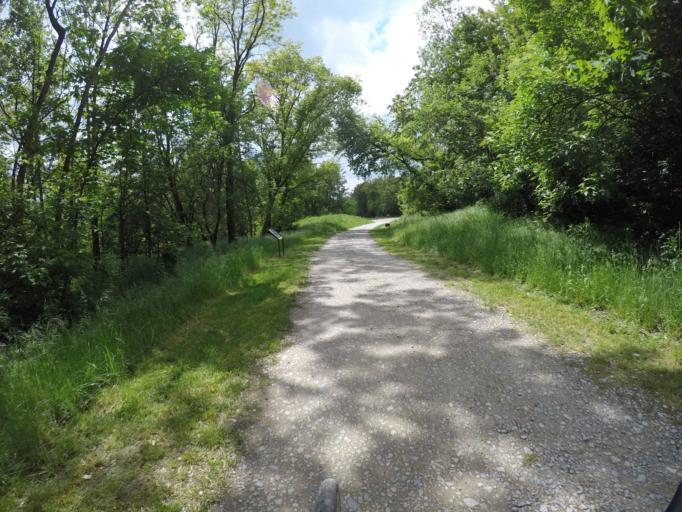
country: DE
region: Berlin
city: Kaulsdorf
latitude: 52.5330
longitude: 13.5823
